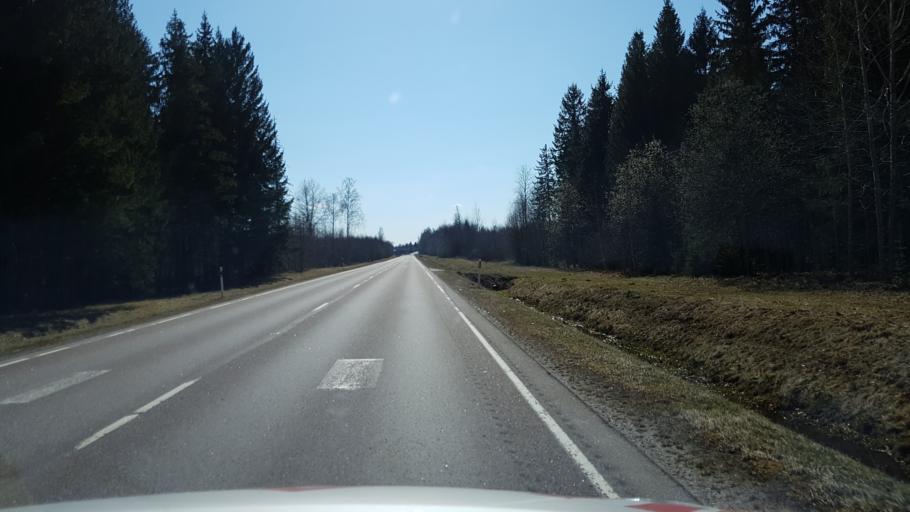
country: EE
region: Jogevamaa
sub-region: Mustvee linn
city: Mustvee
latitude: 58.7623
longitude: 26.8878
